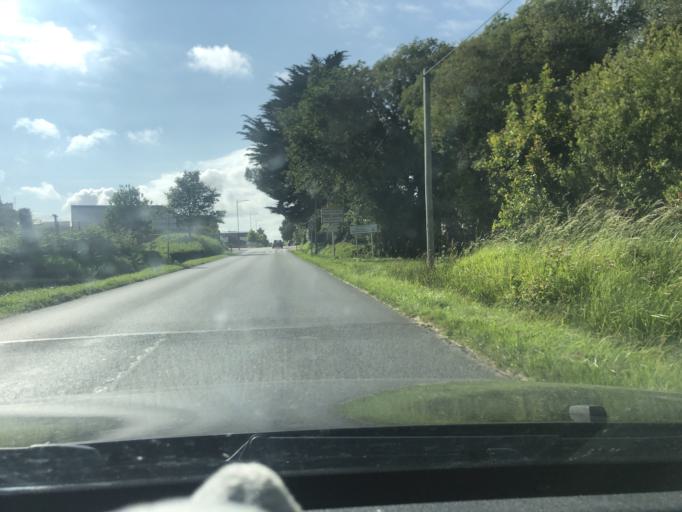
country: FR
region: Brittany
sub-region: Departement du Morbihan
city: Merlevenez
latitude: 47.6934
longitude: -3.2400
